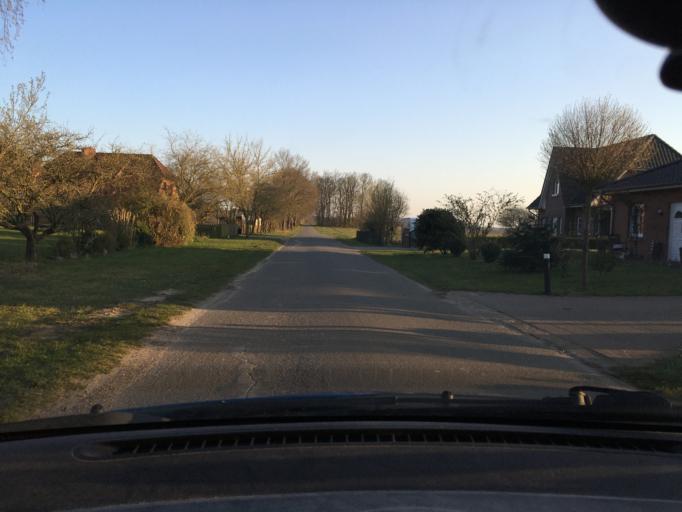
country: DE
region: Lower Saxony
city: Romstedt
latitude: 53.1627
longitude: 10.6639
